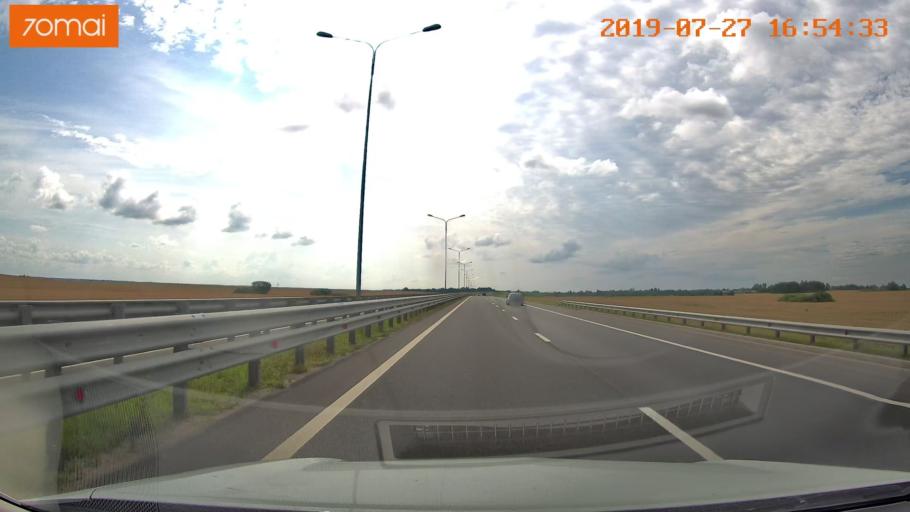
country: RU
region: Kaliningrad
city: Bol'shoe Isakovo
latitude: 54.6932
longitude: 20.8006
